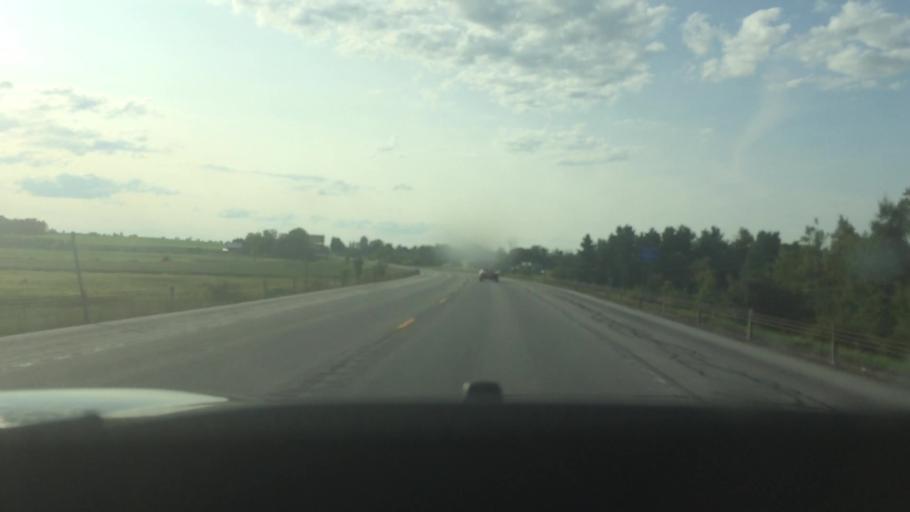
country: US
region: New York
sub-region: St. Lawrence County
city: Canton
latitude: 44.6296
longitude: -75.2412
